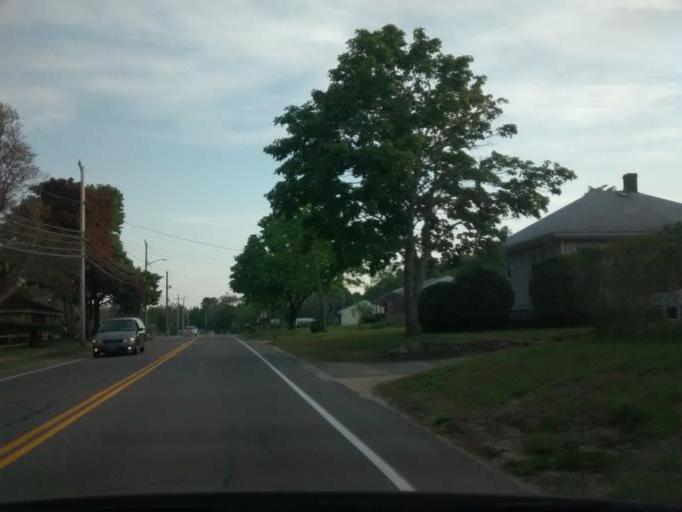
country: US
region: Massachusetts
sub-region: Barnstable County
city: Teaticket
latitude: 41.5786
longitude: -70.5919
